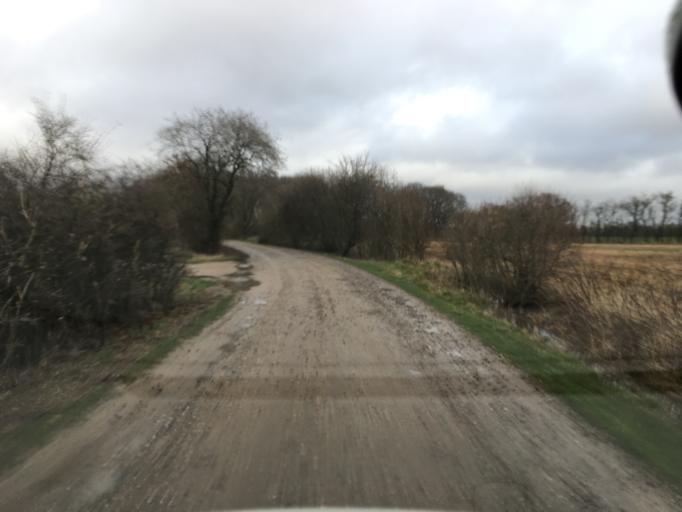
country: DE
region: Schleswig-Holstein
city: Bramstedtlund
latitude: 54.9522
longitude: 9.0467
